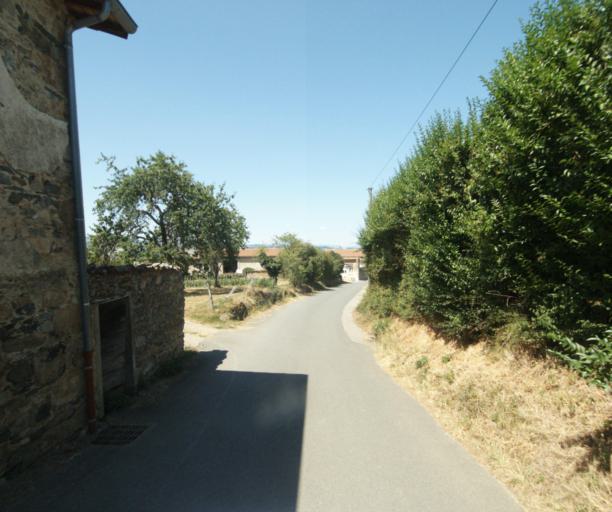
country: FR
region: Rhone-Alpes
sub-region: Departement du Rhone
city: Courzieu
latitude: 45.7572
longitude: 4.5848
